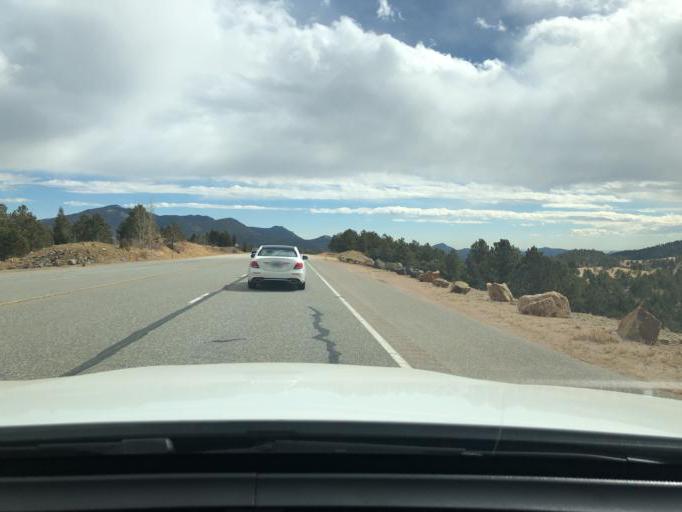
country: US
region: Colorado
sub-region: Gilpin County
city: Central City
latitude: 39.7892
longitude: -105.5034
